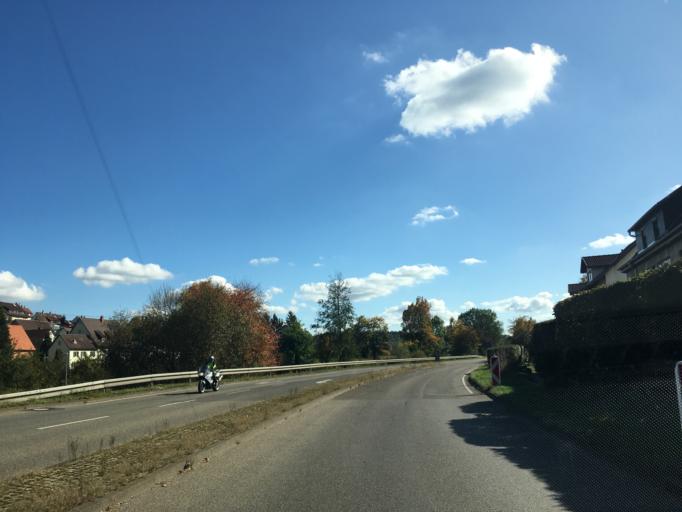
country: DE
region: Baden-Wuerttemberg
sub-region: Regierungsbezirk Stuttgart
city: Weil der Stadt
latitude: 48.7258
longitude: 8.8904
